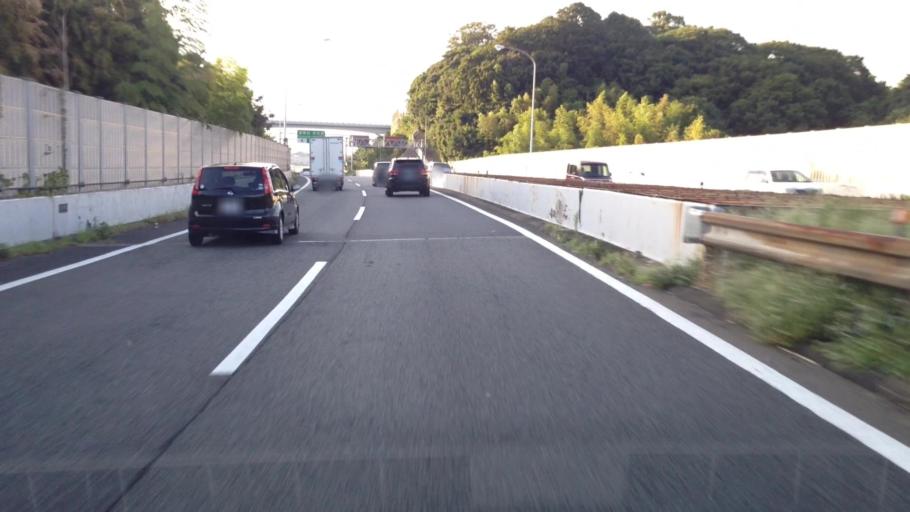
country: JP
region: Kanagawa
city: Kamakura
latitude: 35.3646
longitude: 139.5980
